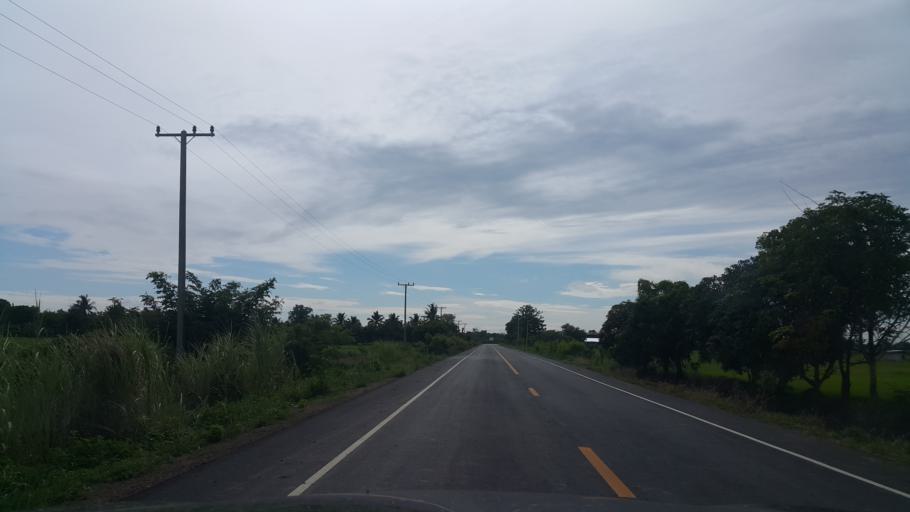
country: TH
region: Sukhothai
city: Si Nakhon
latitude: 17.2726
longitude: 99.9450
